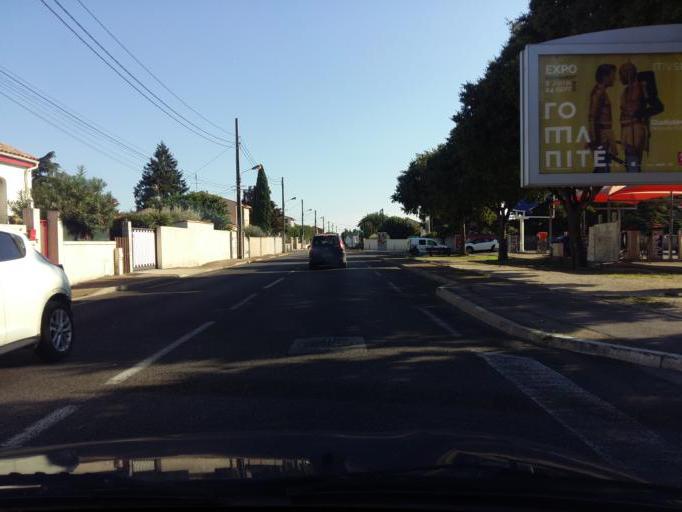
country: FR
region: Languedoc-Roussillon
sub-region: Departement du Gard
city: Nimes
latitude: 43.8177
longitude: 4.3528
